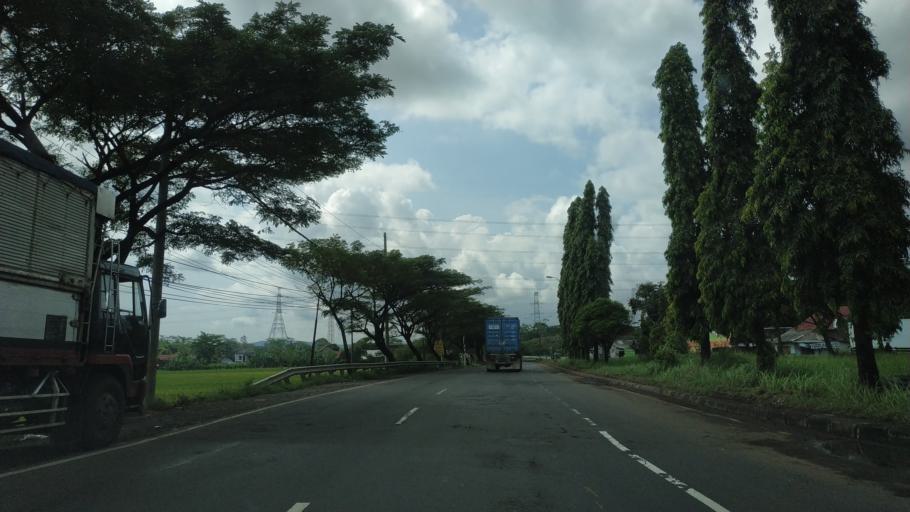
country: ID
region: Central Java
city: Pekalongan
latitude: -6.9502
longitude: 109.7927
